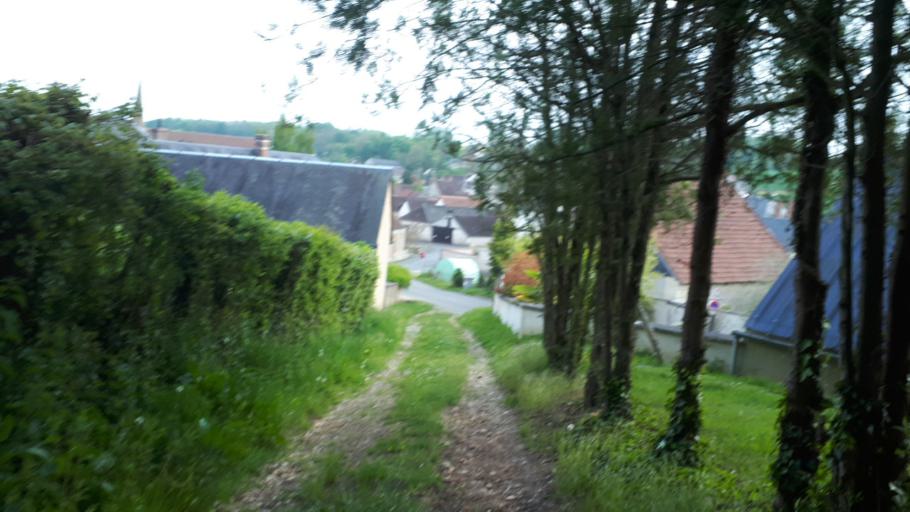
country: FR
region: Centre
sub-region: Departement du Loir-et-Cher
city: Lunay
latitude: 47.8250
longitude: 0.9462
